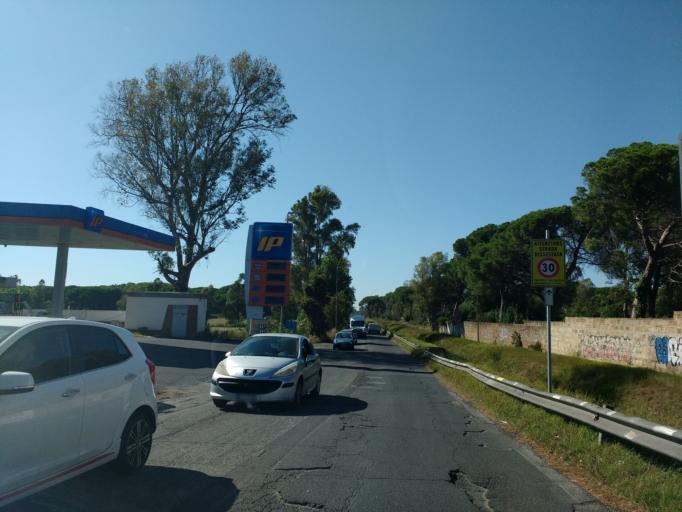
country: IT
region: Latium
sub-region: Citta metropolitana di Roma Capitale
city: Acilia-Castel Fusano-Ostia Antica
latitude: 41.7365
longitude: 12.3455
